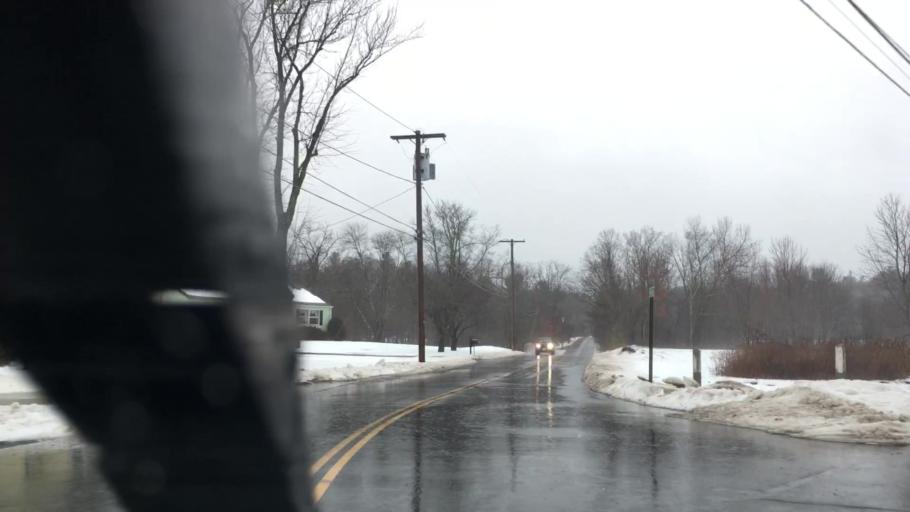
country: US
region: Massachusetts
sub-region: Hampshire County
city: Granby
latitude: 42.2650
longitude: -72.4592
